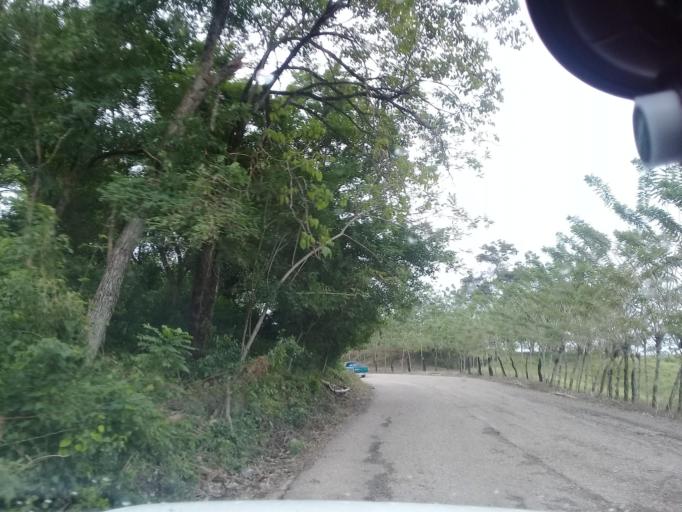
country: MX
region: Veracruz
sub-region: Chalma
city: San Pedro Coyutla
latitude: 21.2122
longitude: -98.3832
